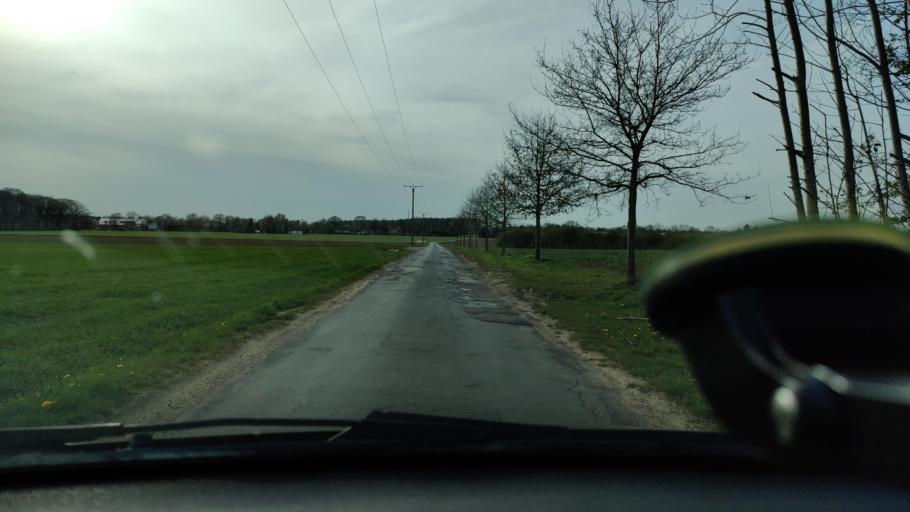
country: DE
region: North Rhine-Westphalia
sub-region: Regierungsbezirk Dusseldorf
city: Kleve
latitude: 51.7433
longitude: 6.1765
